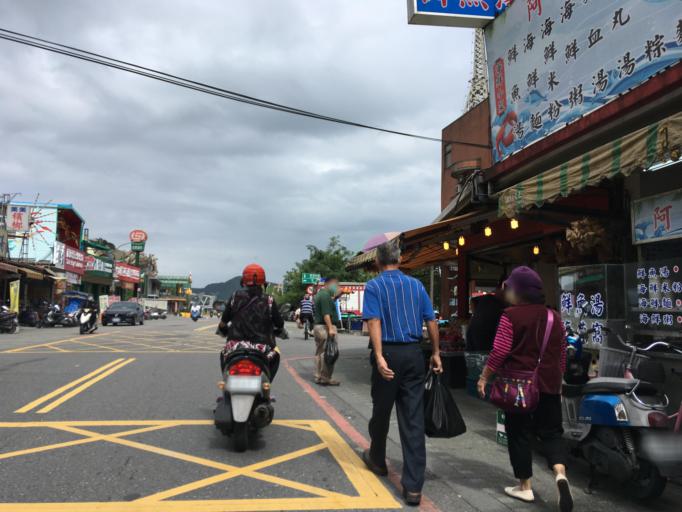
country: TW
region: Taiwan
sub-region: Yilan
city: Yilan
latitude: 24.5829
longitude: 121.8649
